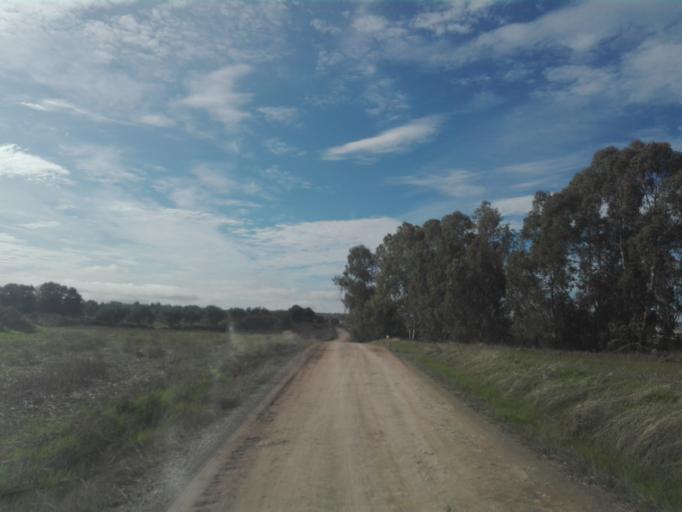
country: ES
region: Extremadura
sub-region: Provincia de Badajoz
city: Villagarcia de la Torre
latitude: 38.3078
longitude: -6.0826
